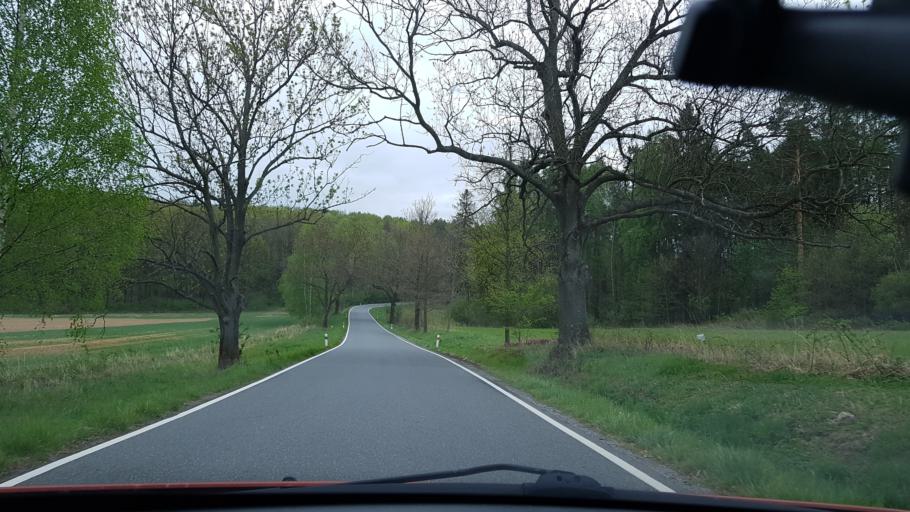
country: CZ
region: Olomoucky
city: Vidnava
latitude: 50.3622
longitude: 17.2045
